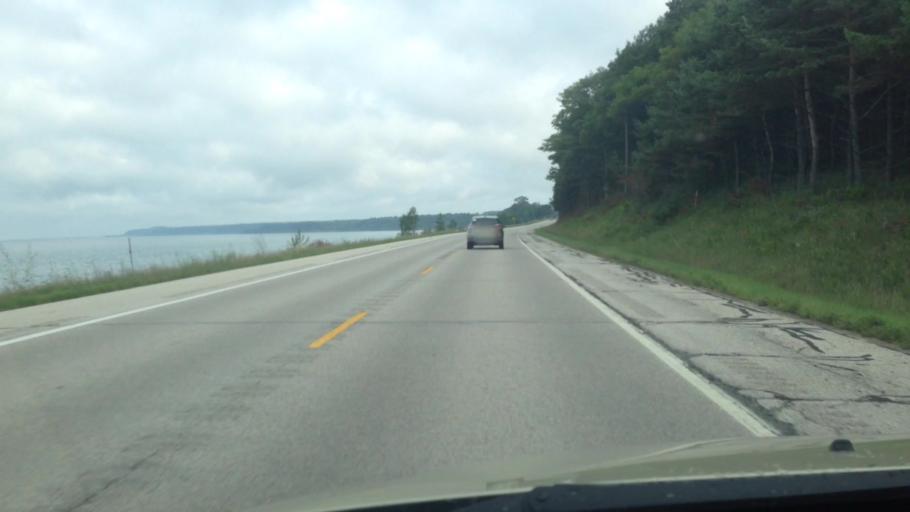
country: US
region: Michigan
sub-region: Mackinac County
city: Saint Ignace
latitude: 45.9964
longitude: -84.9890
